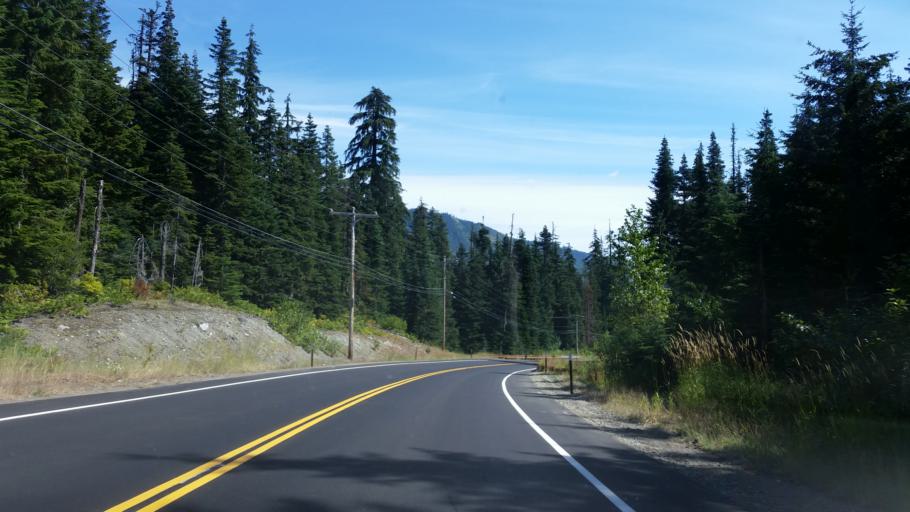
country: US
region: Washington
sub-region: King County
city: Tanner
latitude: 47.4045
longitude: -121.4096
